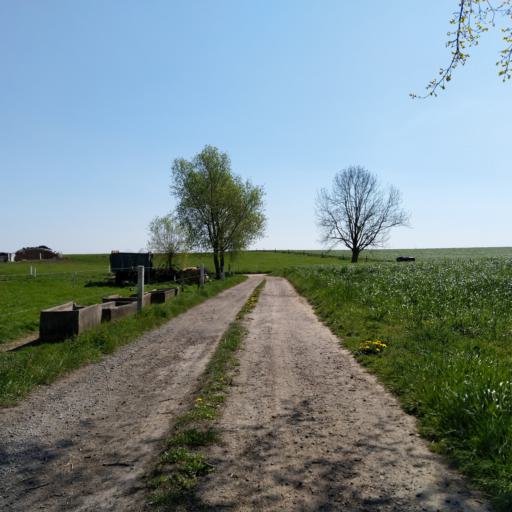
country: BE
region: Wallonia
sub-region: Province du Hainaut
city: Lens
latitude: 50.5955
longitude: 3.9249
